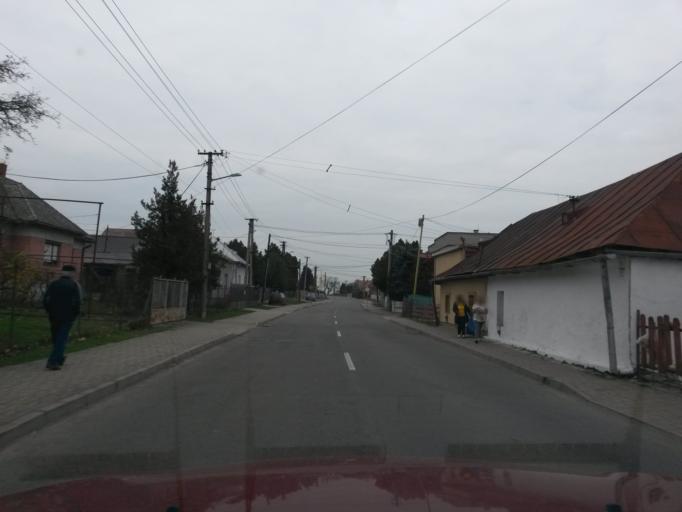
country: SK
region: Kosicky
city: Secovce
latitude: 48.7042
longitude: 21.6538
